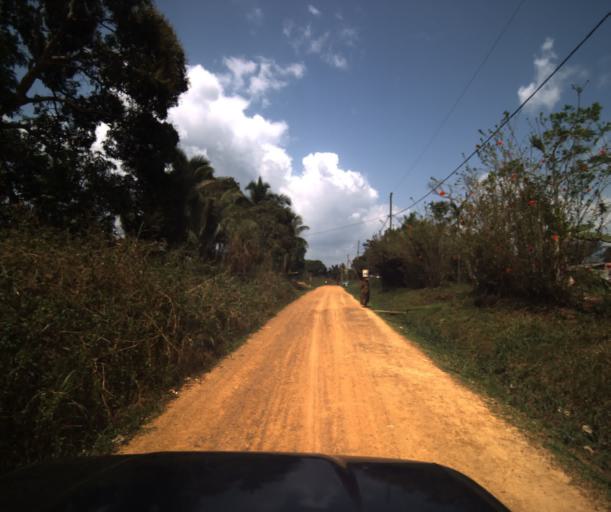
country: CM
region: Centre
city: Eseka
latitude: 3.5419
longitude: 11.0214
